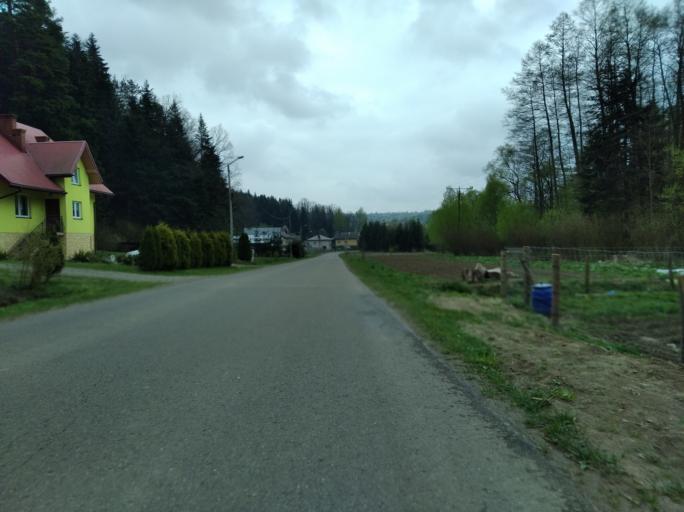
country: PL
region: Subcarpathian Voivodeship
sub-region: Powiat brzozowski
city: Jablonka
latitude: 49.7419
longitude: 22.0787
